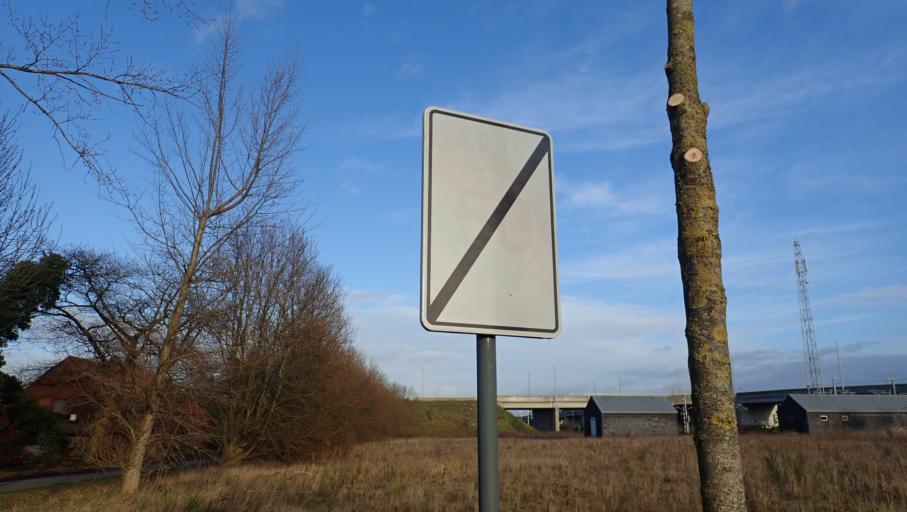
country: BE
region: Flanders
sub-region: Provincie Antwerpen
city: Brecht
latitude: 51.3584
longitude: 4.6328
